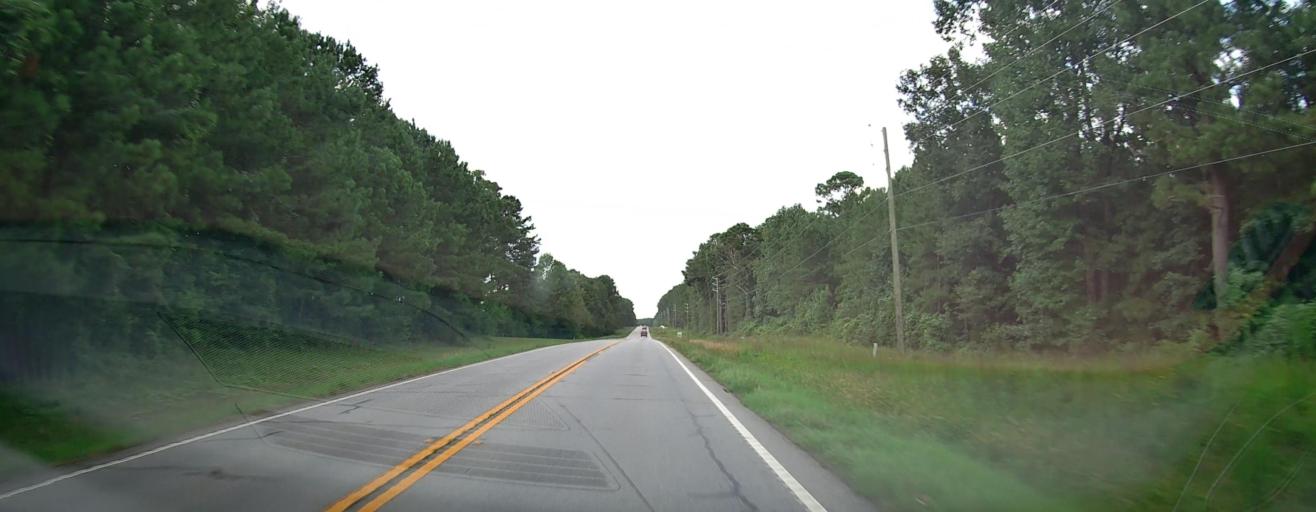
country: US
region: Georgia
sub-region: Meriwether County
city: Greenville
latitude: 33.0723
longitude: -84.5720
